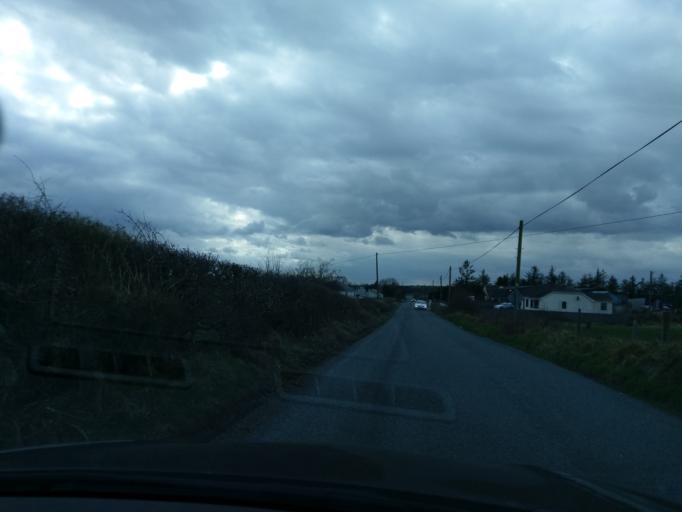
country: IE
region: Connaught
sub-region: County Galway
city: Athenry
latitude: 53.4730
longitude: -8.6514
